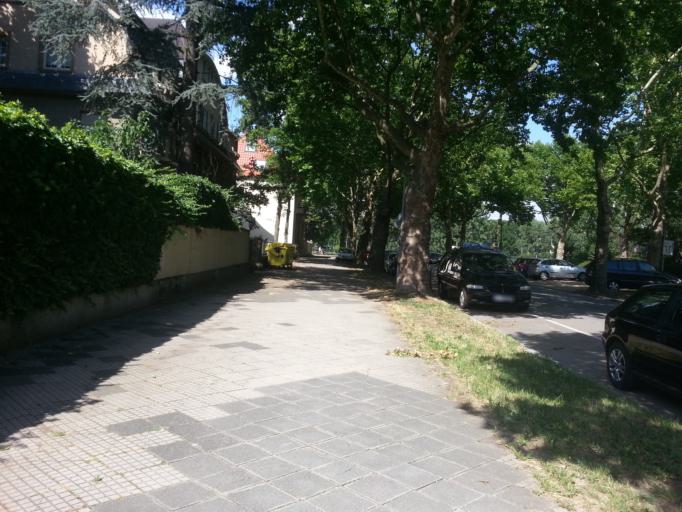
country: DE
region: Baden-Wuerttemberg
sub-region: Karlsruhe Region
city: Mannheim
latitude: 49.4872
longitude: 8.4890
